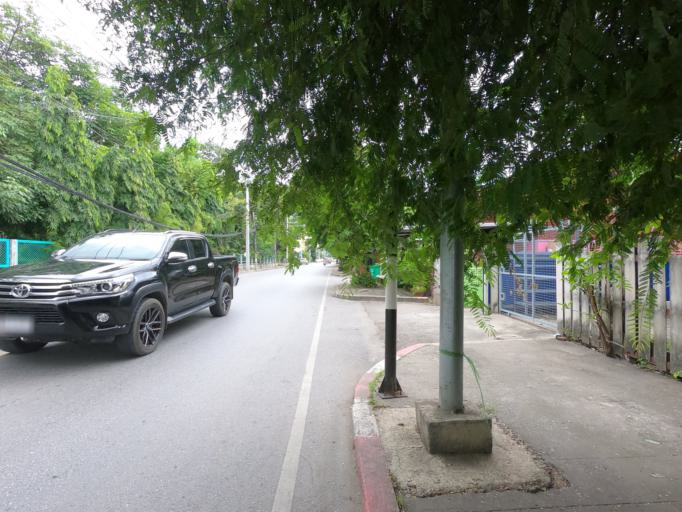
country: TH
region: Nakhon Pathom
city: Nakhon Pathom
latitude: 13.8199
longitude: 100.0505
